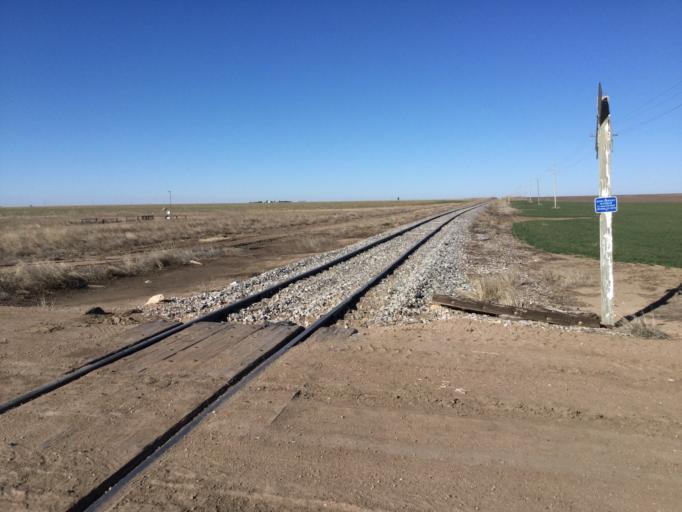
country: US
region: Kansas
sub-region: Grant County
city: Ulysses
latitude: 37.5620
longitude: -101.4718
